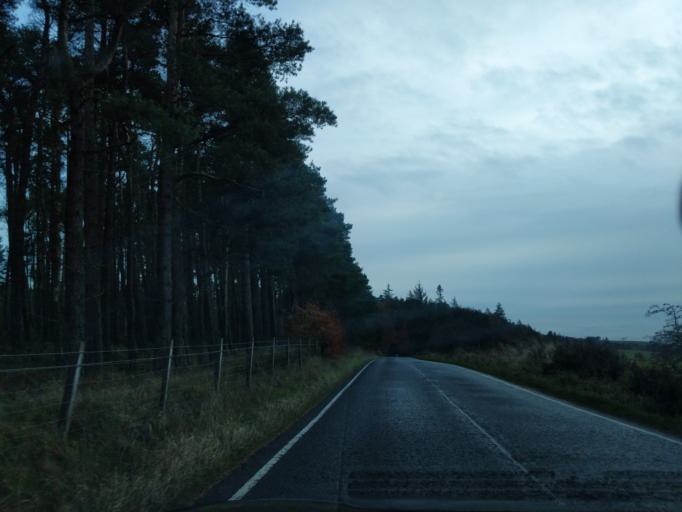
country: GB
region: Scotland
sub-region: West Lothian
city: Linlithgow
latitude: 55.9470
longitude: -3.6154
